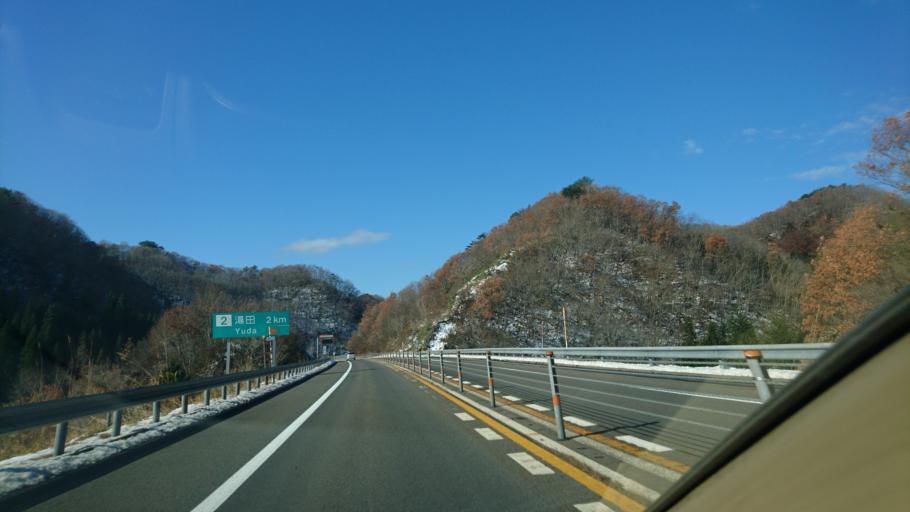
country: JP
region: Akita
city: Yokotemachi
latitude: 39.3138
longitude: 140.7704
